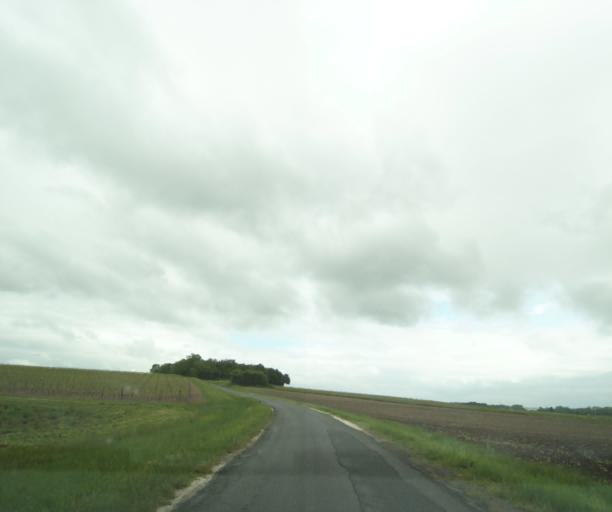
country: FR
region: Poitou-Charentes
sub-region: Departement de la Charente-Maritime
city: Perignac
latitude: 45.6709
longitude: -0.4960
